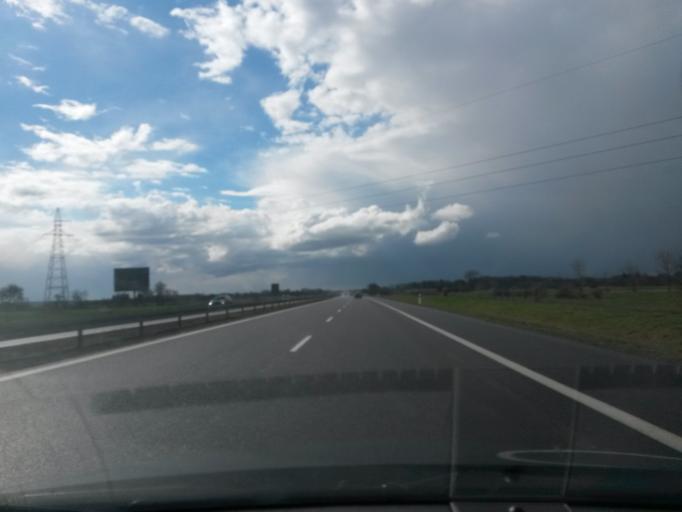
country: PL
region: Greater Poland Voivodeship
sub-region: Powiat wrzesinski
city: Wrzesnia
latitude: 52.3181
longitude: 17.5079
